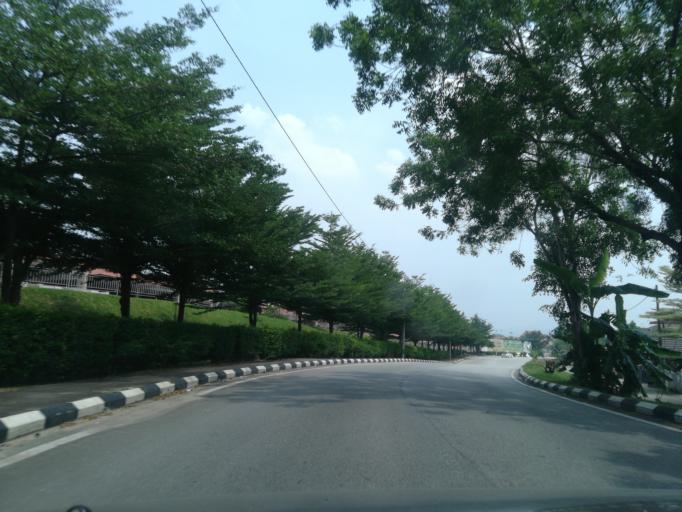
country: MY
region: Kedah
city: Kulim
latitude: 5.3996
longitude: 100.5677
